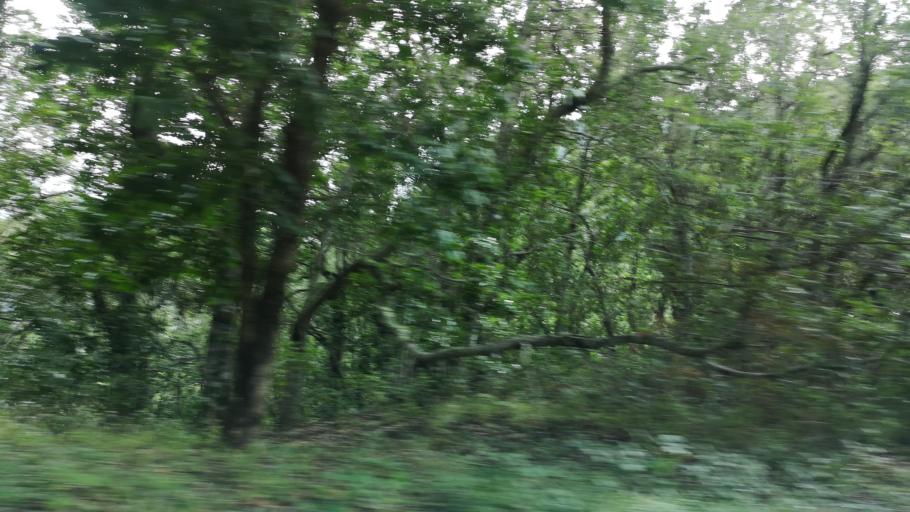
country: ES
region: Canary Islands
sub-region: Provincia de Santa Cruz de Tenerife
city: Hermigua
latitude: 28.1269
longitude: -17.2112
